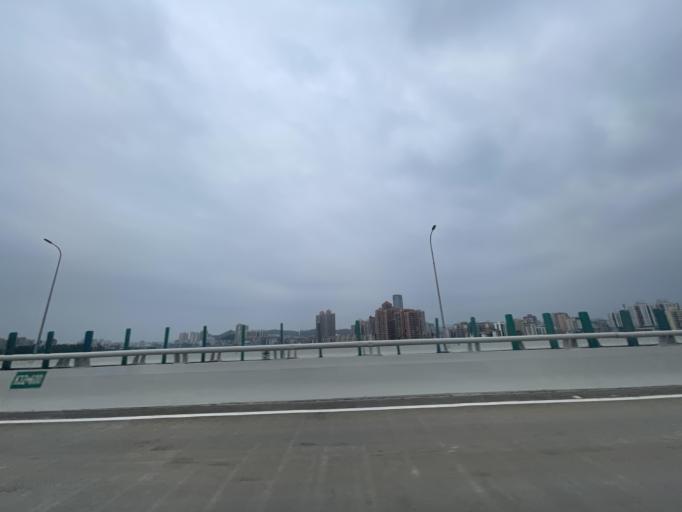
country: CN
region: Guangdong
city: Humen
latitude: 22.8067
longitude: 113.6664
